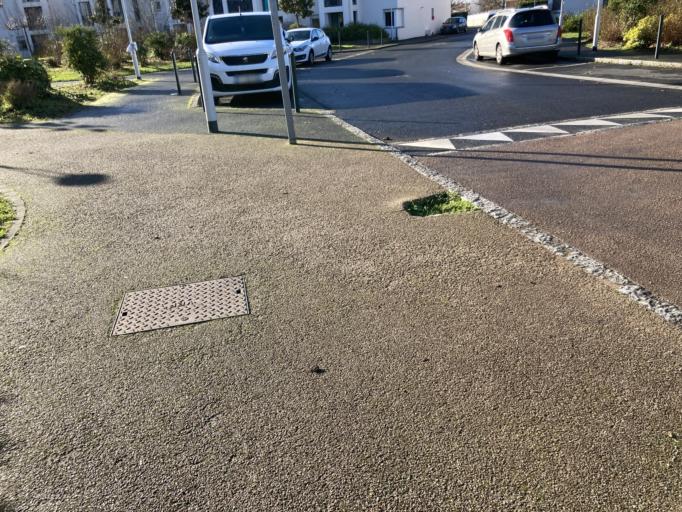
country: FR
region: Pays de la Loire
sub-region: Departement de la Loire-Atlantique
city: Saint-Sebastien-sur-Loire
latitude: 47.2039
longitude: -1.4865
